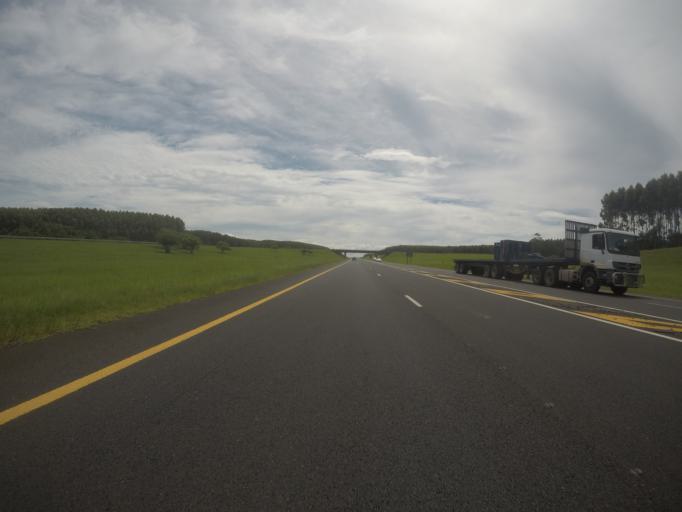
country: ZA
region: KwaZulu-Natal
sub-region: uThungulu District Municipality
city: Eshowe
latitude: -29.0421
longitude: 31.6473
